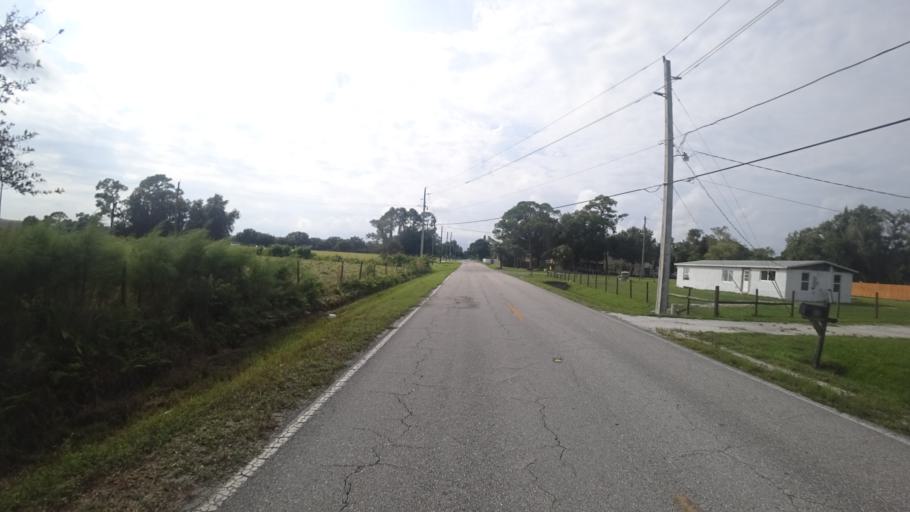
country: US
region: Florida
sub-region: Manatee County
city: Samoset
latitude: 27.4657
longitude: -82.5379
